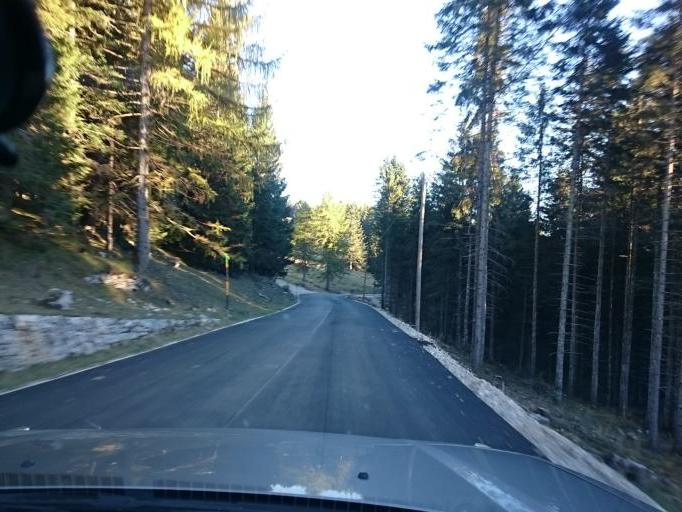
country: IT
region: Trentino-Alto Adige
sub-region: Provincia di Trento
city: Novaledo
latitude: 45.9652
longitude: 11.4162
